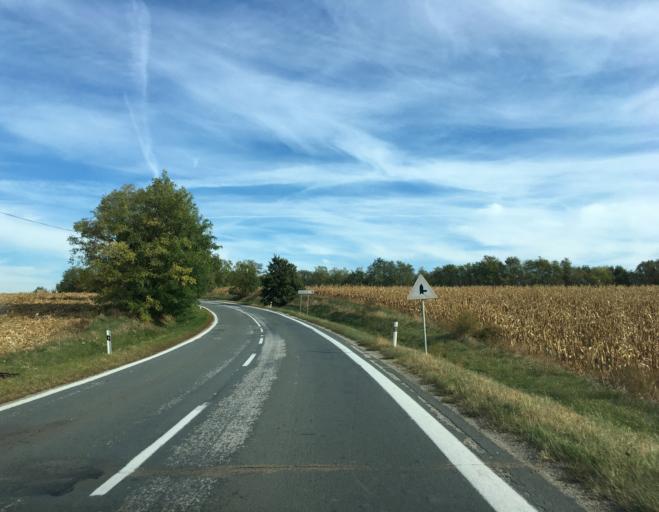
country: SK
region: Nitriansky
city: Svodin
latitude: 48.0322
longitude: 18.4232
